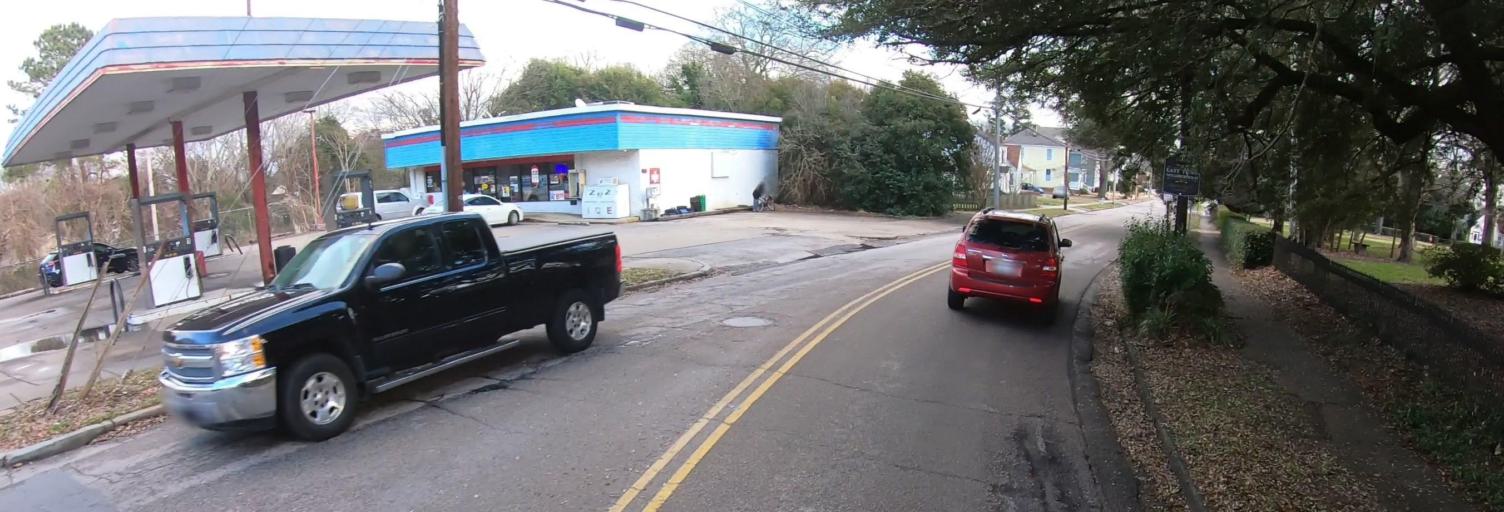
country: US
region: South Carolina
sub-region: York County
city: Rock Hill
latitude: 34.9258
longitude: -81.0221
